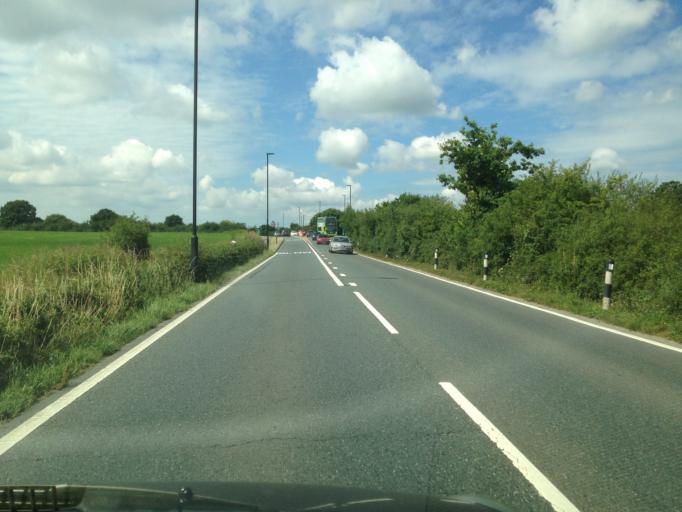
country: GB
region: England
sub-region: Isle of Wight
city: Newport
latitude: 50.7225
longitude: -1.2659
